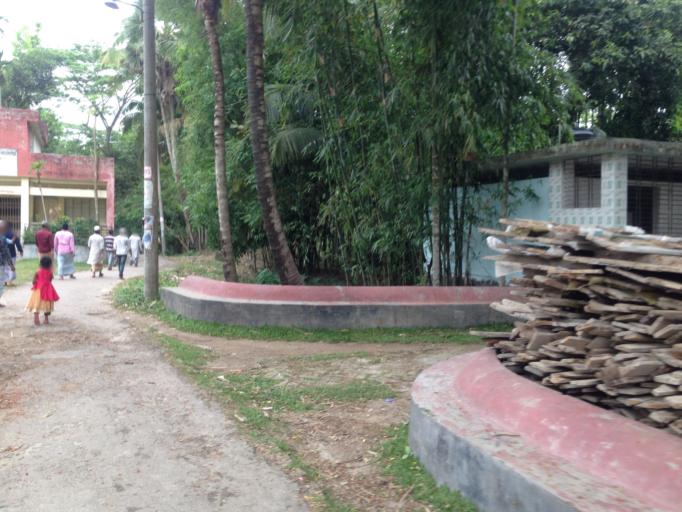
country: BD
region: Chittagong
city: Raipur
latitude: 23.0348
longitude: 90.7715
